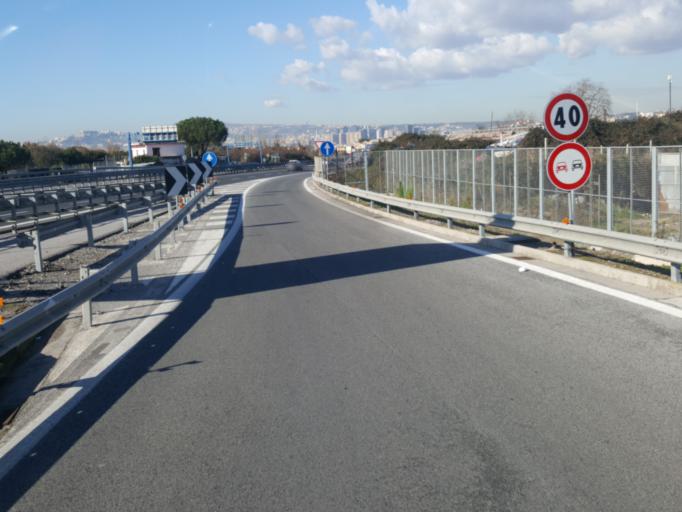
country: IT
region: Campania
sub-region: Provincia di Napoli
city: San Giorgio a Cremano
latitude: 40.8425
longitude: 14.3279
